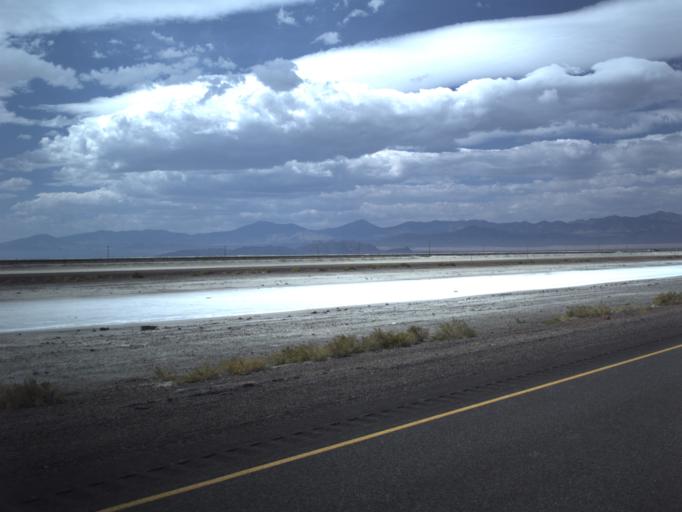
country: US
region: Utah
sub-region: Tooele County
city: Wendover
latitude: 40.7409
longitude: -113.9281
